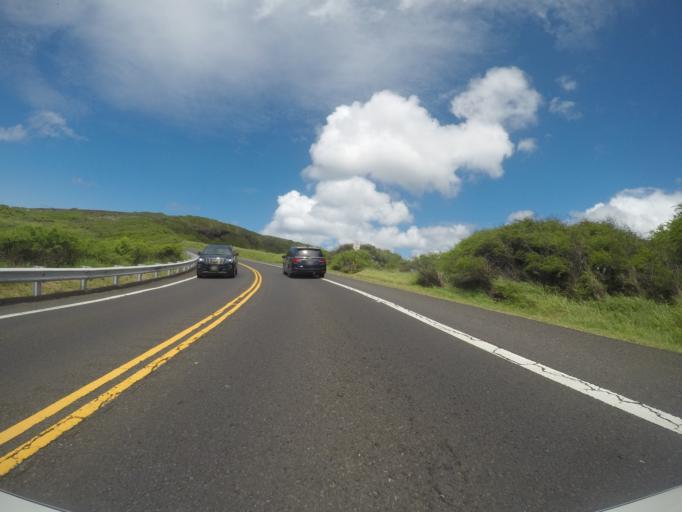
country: US
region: Hawaii
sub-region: Honolulu County
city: Waimanalo Beach
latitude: 21.2766
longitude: -157.6873
